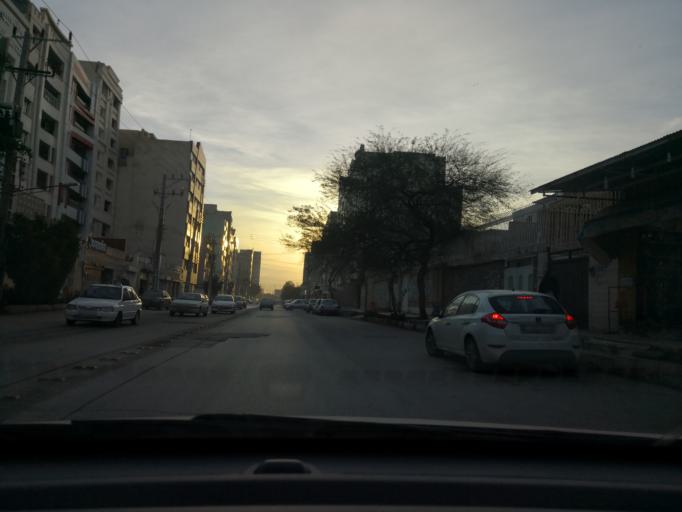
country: IR
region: Khuzestan
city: Ahvaz
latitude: 31.3495
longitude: 48.6899
